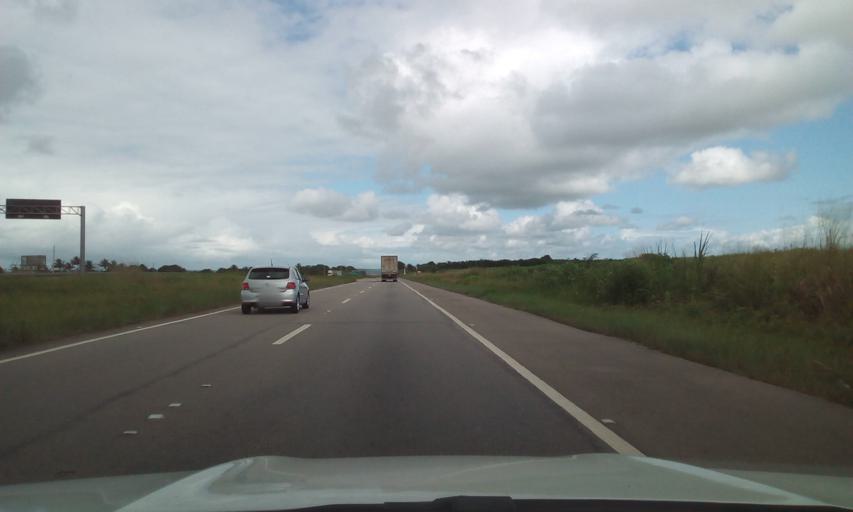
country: BR
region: Pernambuco
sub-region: Itapissuma
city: Itapissuma
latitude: -7.6731
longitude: -34.9304
